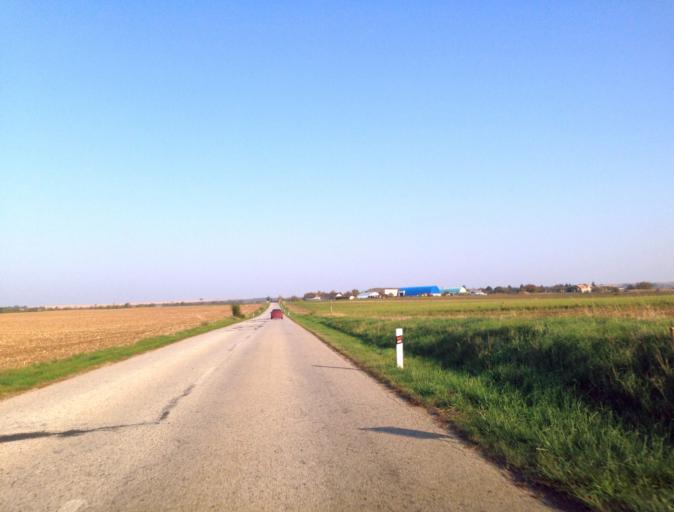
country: SK
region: Nitriansky
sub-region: Okres Komarno
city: Hurbanovo
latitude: 47.8935
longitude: 18.2361
